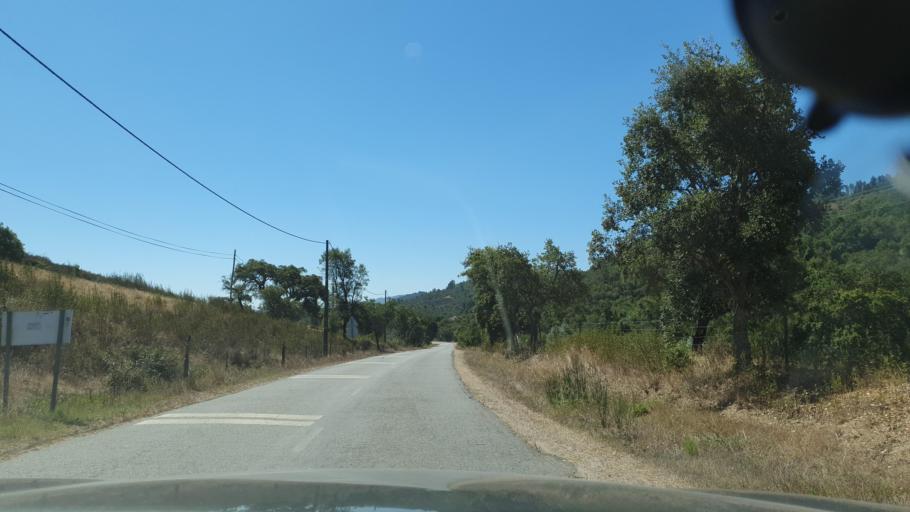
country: PT
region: Beja
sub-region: Odemira
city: Sao Teotonio
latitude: 37.4987
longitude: -8.6528
